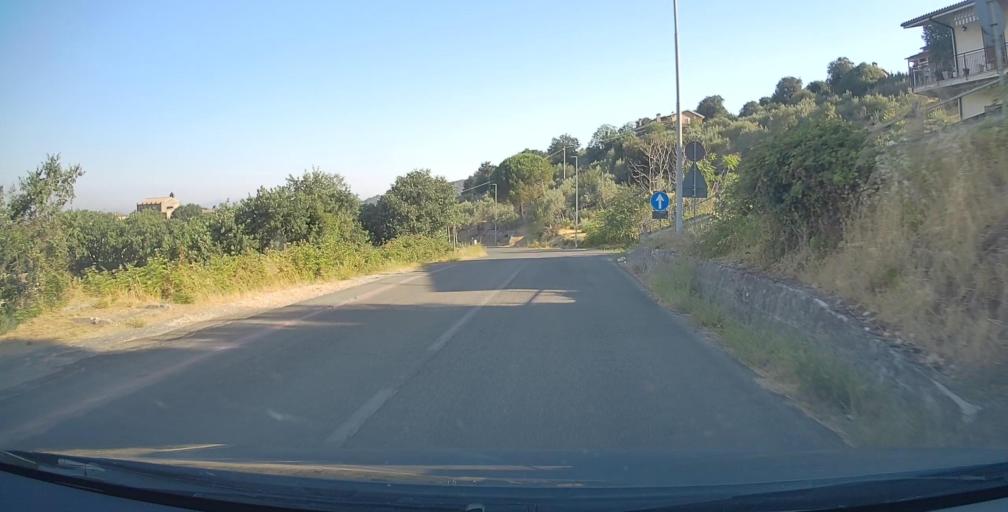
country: IT
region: Umbria
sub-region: Provincia di Terni
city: Calvi dell'Umbria
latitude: 42.4053
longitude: 12.5658
